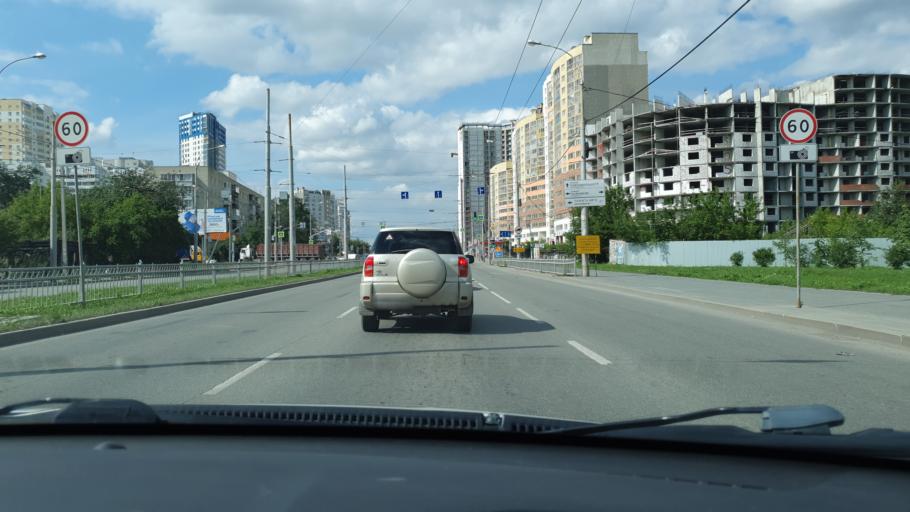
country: RU
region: Sverdlovsk
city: Yekaterinburg
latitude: 56.7806
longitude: 60.6567
